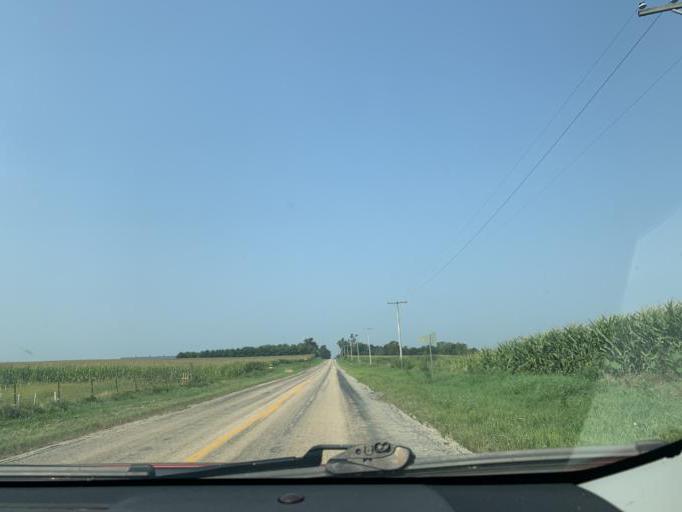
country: US
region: Illinois
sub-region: Whiteside County
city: Morrison
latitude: 41.8480
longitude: -89.8484
